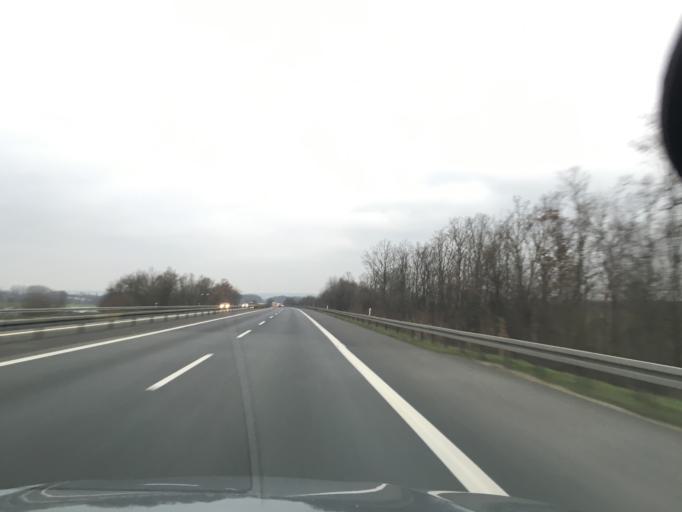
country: DE
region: Bavaria
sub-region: Regierungsbezirk Unterfranken
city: Kleinlangheim
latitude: 49.7789
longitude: 10.3006
